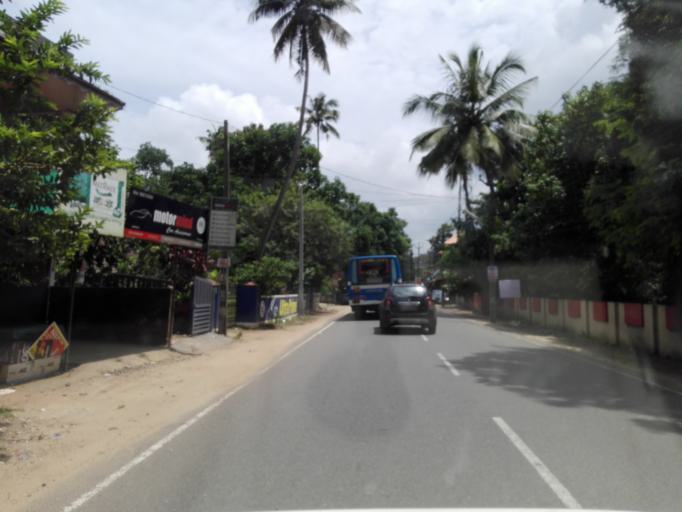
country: IN
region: Kerala
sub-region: Alappuzha
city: Arukutti
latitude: 9.8507
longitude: 76.3856
